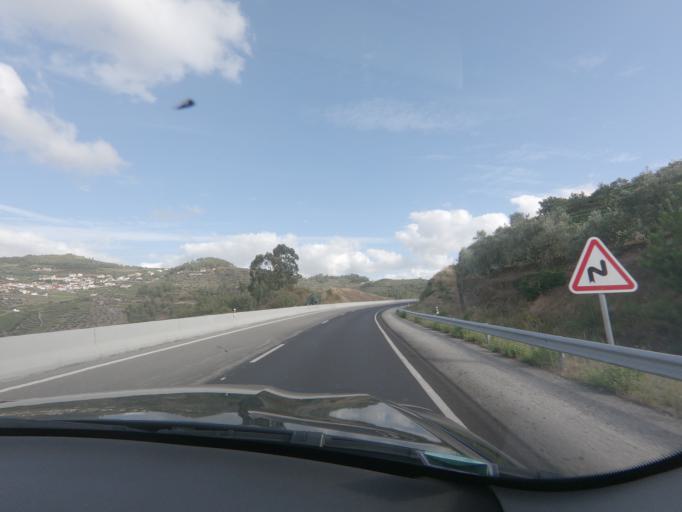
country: PT
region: Viseu
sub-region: Lamego
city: Lamego
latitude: 41.1048
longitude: -7.7753
